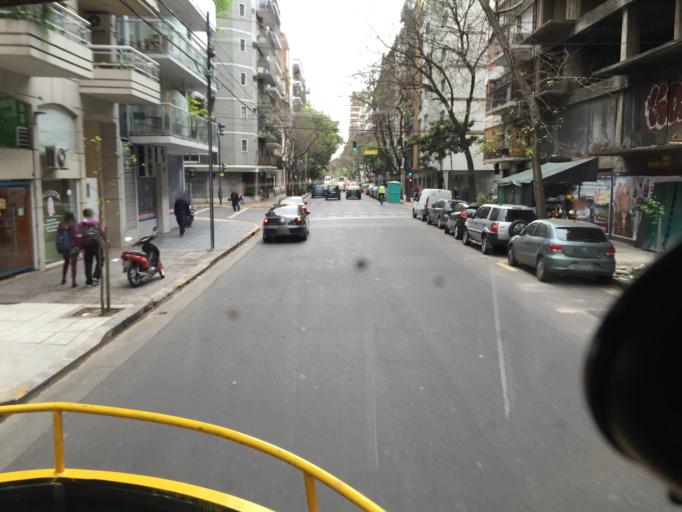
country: AR
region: Buenos Aires F.D.
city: Retiro
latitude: -34.5876
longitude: -58.4033
